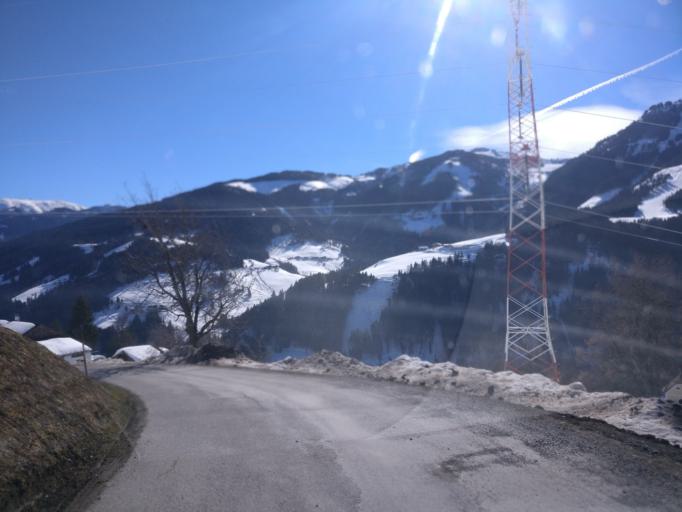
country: AT
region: Salzburg
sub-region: Politischer Bezirk Sankt Johann im Pongau
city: Sankt Johann im Pongau
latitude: 47.3363
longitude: 13.2325
